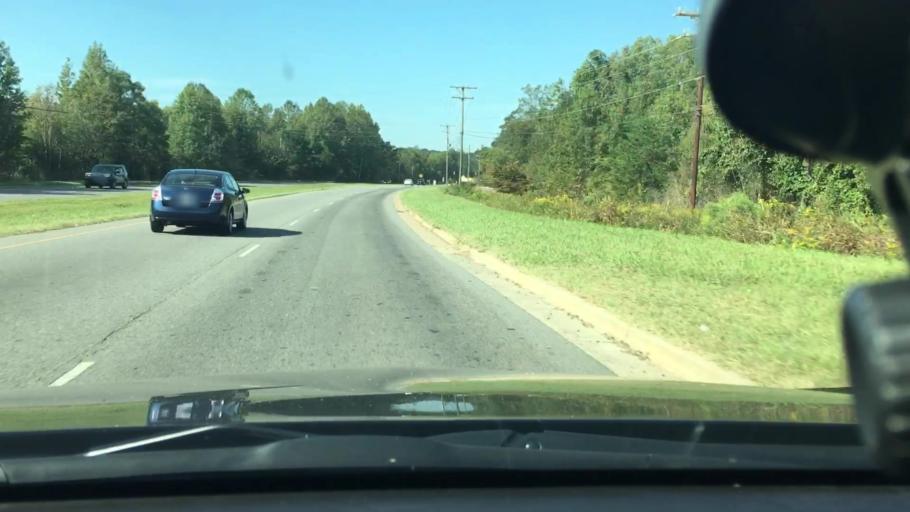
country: US
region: North Carolina
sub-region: Mecklenburg County
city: Mint Hill
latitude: 35.2250
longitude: -80.6160
